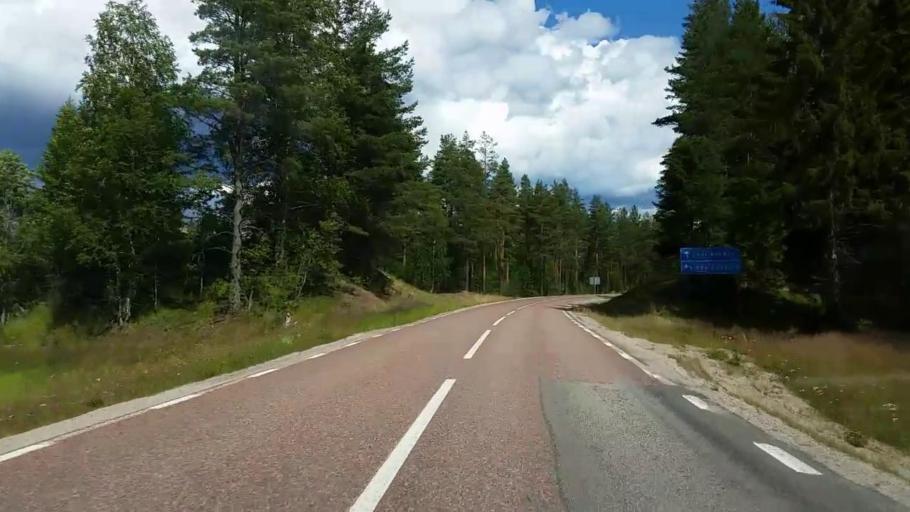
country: SE
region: Gaevleborg
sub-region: Ovanakers Kommun
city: Edsbyn
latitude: 61.3420
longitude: 15.5458
